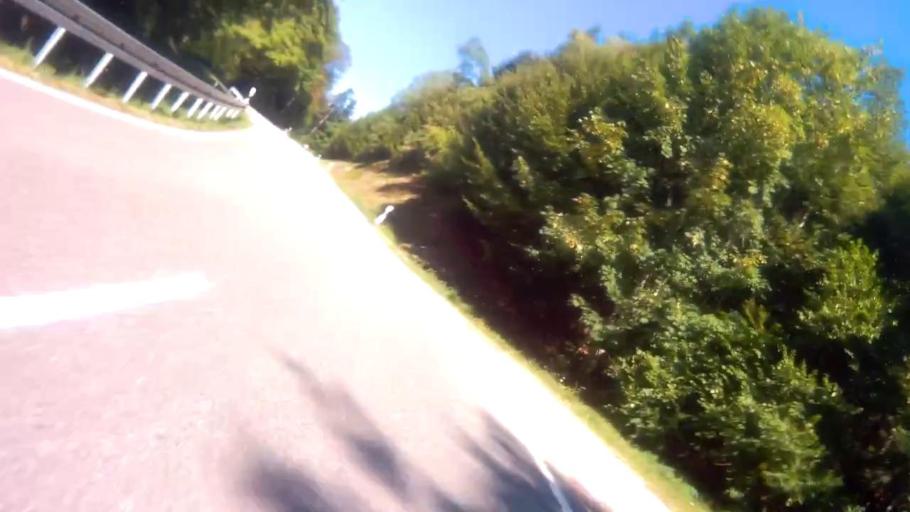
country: DE
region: Baden-Wuerttemberg
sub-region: Freiburg Region
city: Badenweiler
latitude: 47.7826
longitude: 7.7319
